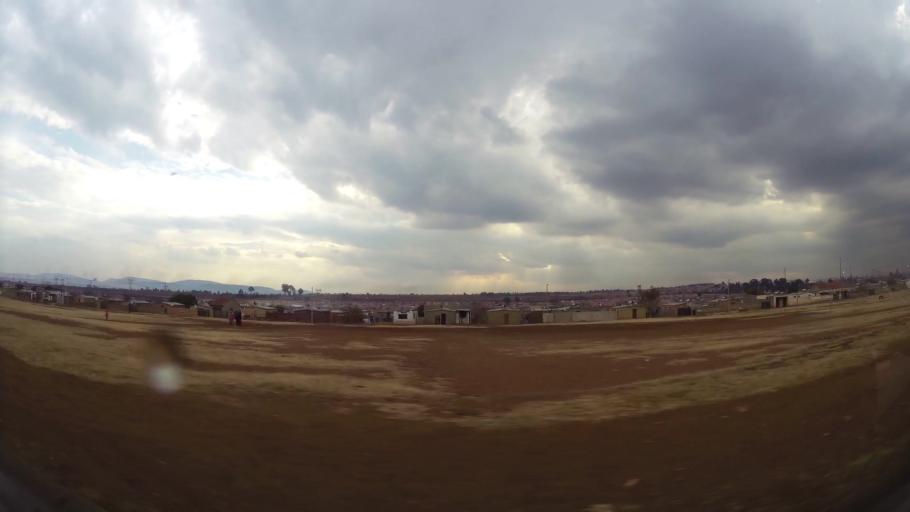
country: ZA
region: Gauteng
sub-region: Ekurhuleni Metropolitan Municipality
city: Germiston
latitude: -26.3740
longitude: 28.1210
